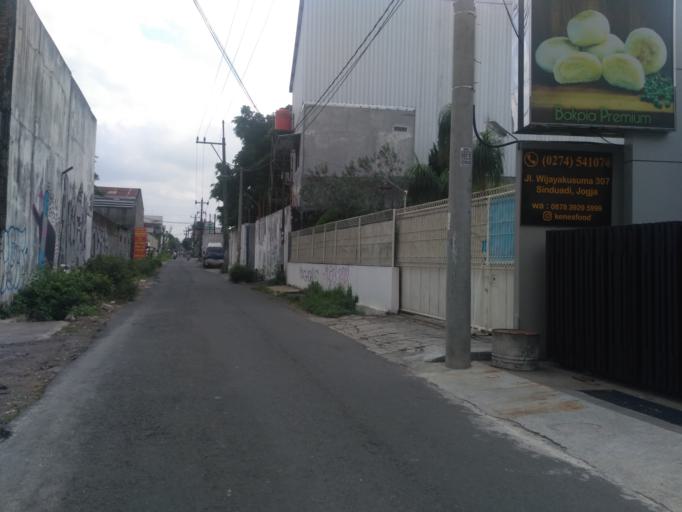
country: ID
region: Daerah Istimewa Yogyakarta
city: Yogyakarta
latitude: -7.7581
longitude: 110.3630
